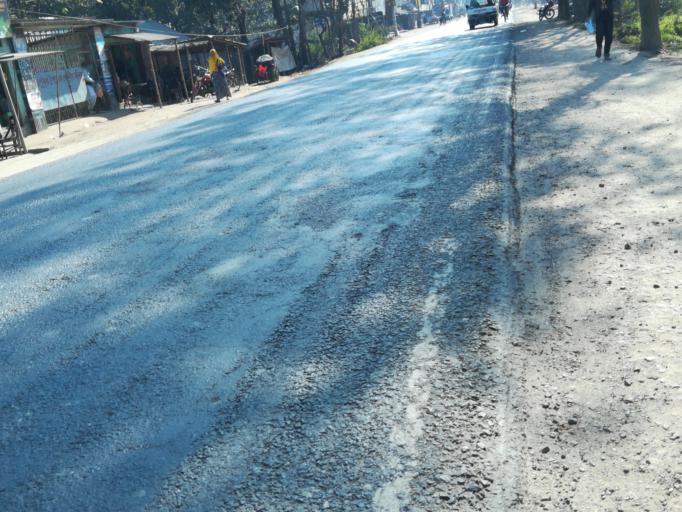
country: BD
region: Rangpur Division
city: Rangpur
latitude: 25.5733
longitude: 89.2745
